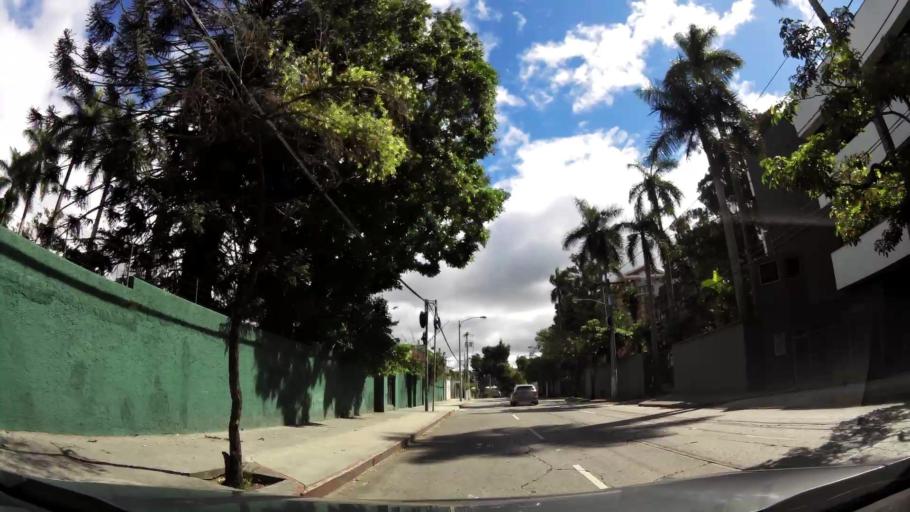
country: GT
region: Guatemala
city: Guatemala City
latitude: 14.6089
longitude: -90.5170
